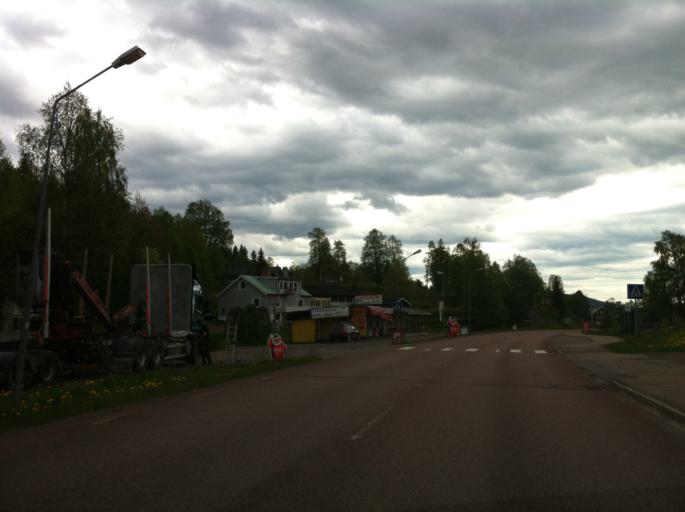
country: SE
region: Dalarna
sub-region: Malung-Saelens kommun
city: Malung
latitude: 61.0970
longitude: 13.3150
